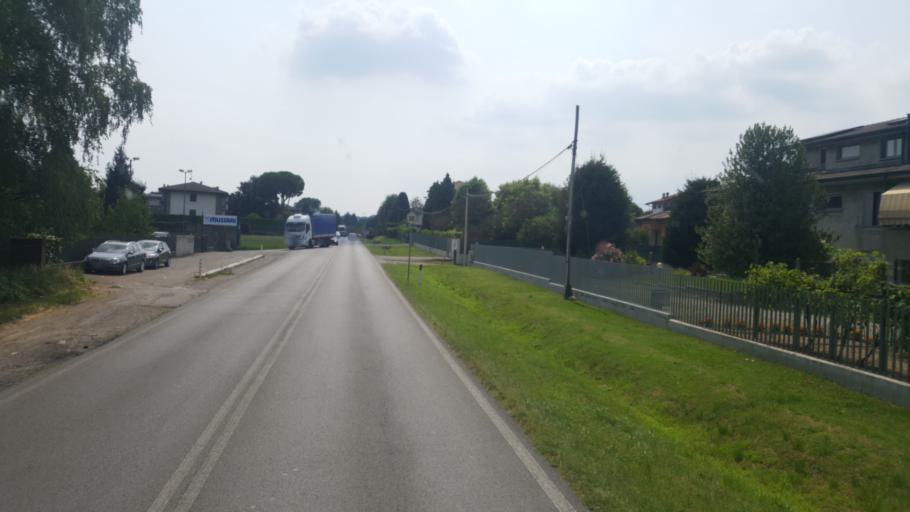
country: IT
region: Lombardy
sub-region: Provincia di Como
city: Lurate Caccivio
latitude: 45.7618
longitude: 9.0059
